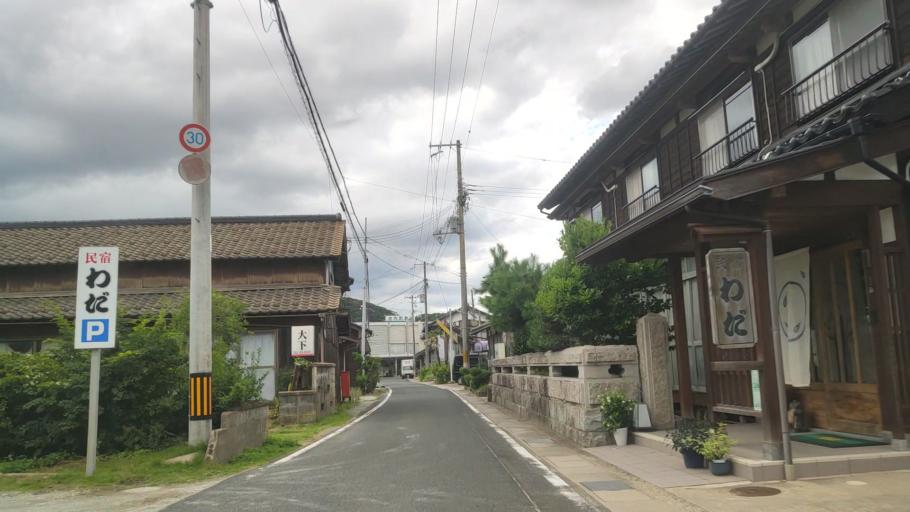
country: JP
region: Hyogo
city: Toyooka
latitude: 35.6426
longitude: 134.9066
